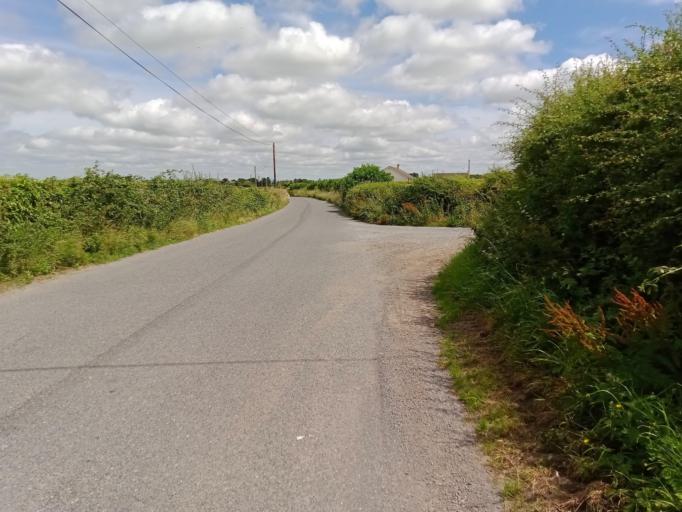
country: IE
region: Leinster
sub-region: Kilkenny
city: Callan
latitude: 52.5450
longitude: -7.4126
